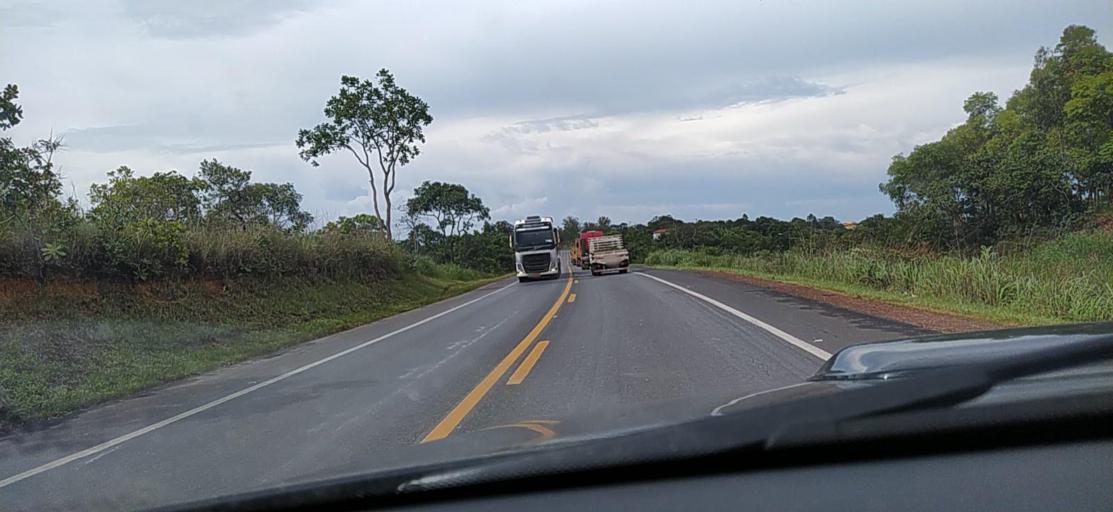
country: BR
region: Minas Gerais
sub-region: Montes Claros
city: Montes Claros
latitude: -16.8437
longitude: -43.8504
